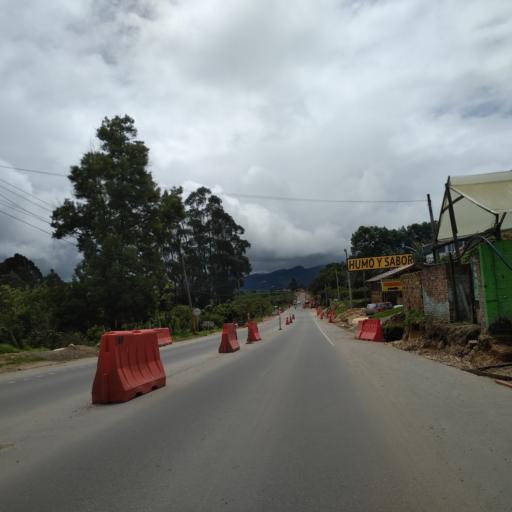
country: CO
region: Cundinamarca
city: La Calera
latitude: 4.7011
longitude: -73.9814
